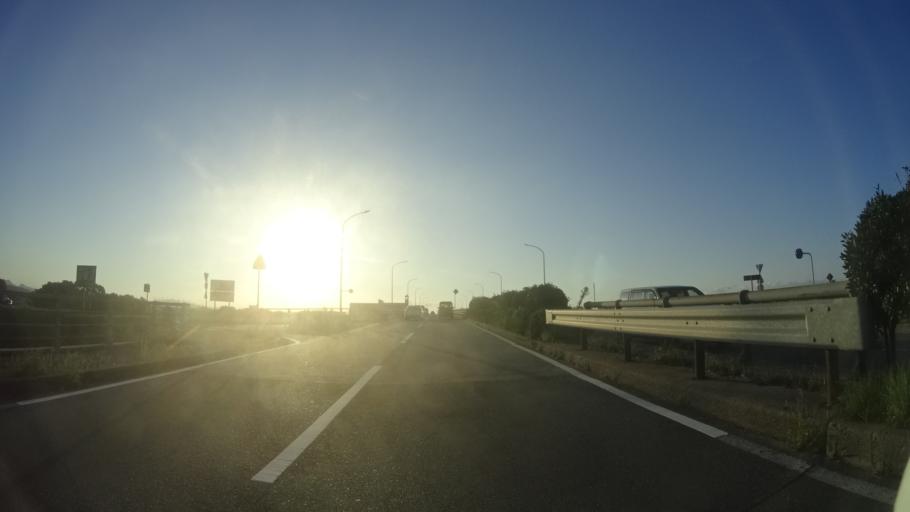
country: JP
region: Tottori
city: Yonago
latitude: 35.4475
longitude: 133.3740
